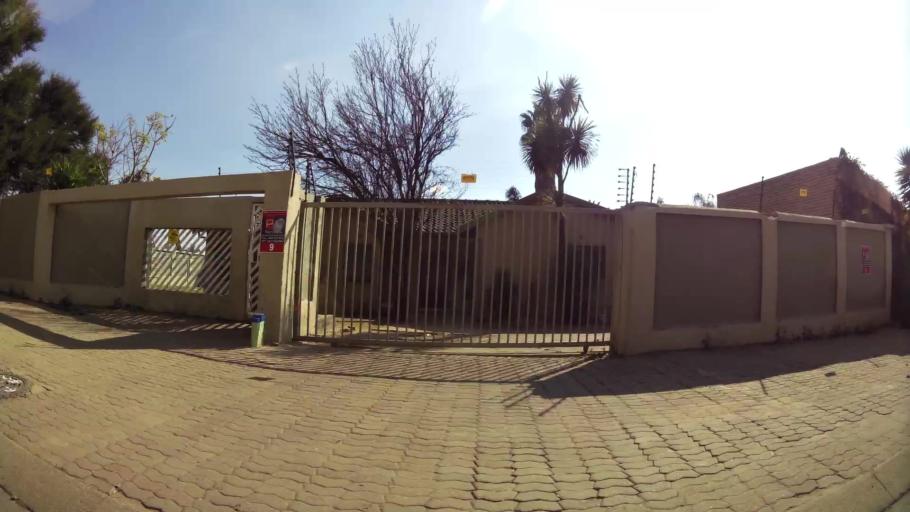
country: ZA
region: Gauteng
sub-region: Ekurhuleni Metropolitan Municipality
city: Tembisa
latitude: -26.0757
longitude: 28.2526
